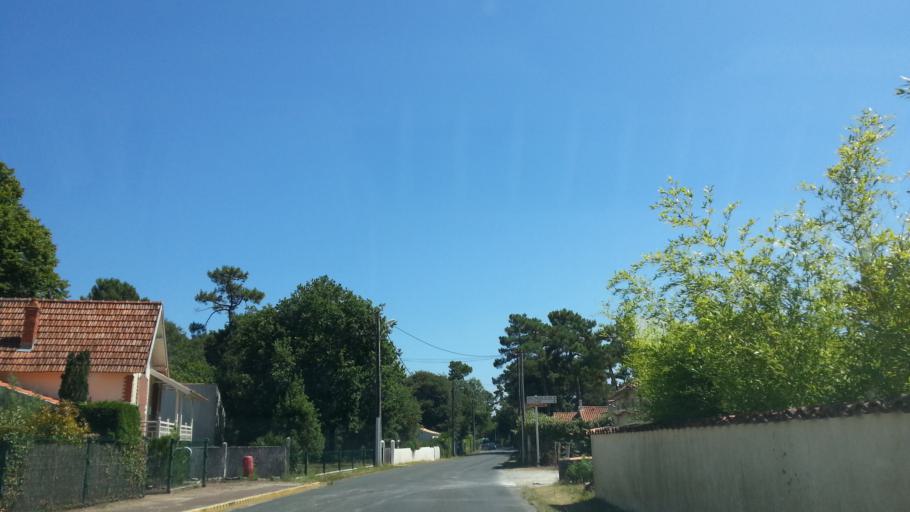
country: FR
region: Poitou-Charentes
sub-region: Departement de la Charente-Maritime
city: Dolus-d'Oleron
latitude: 45.8825
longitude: -1.2554
